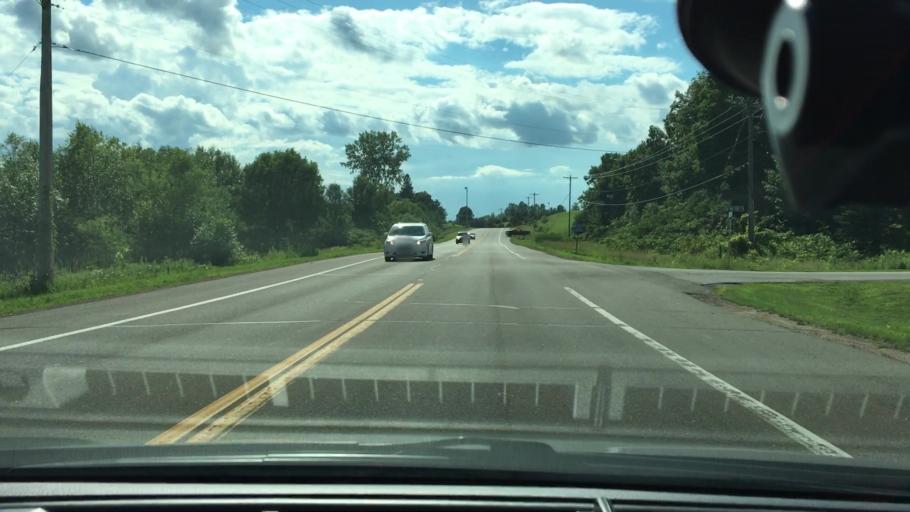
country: US
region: Minnesota
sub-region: Hennepin County
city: Minnetrista
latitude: 44.9244
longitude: -93.7089
